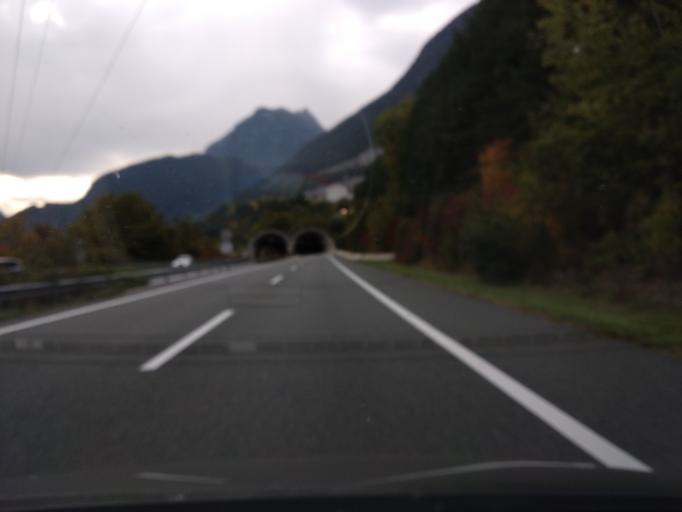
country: AT
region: Tyrol
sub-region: Politischer Bezirk Landeck
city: Schonwies
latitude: 47.1993
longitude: 10.6553
